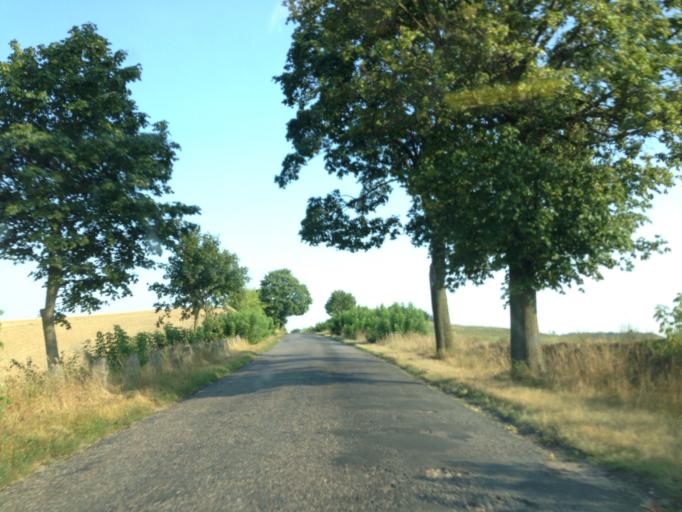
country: PL
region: Warmian-Masurian Voivodeship
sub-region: Powiat nowomiejski
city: Biskupiec
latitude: 53.4666
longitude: 19.2657
